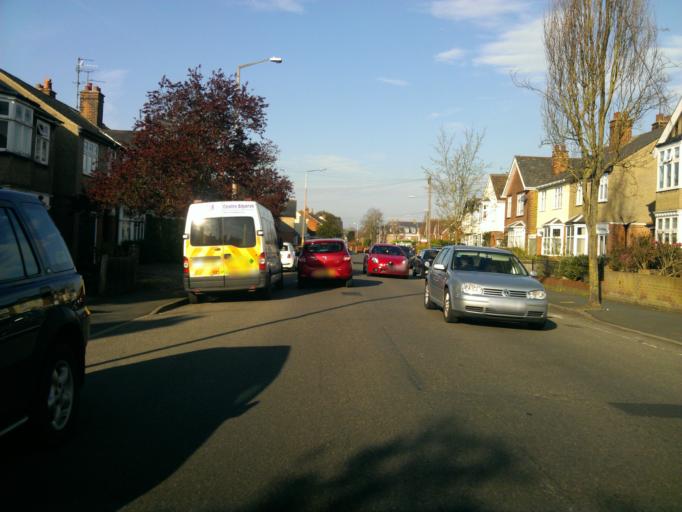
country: GB
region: England
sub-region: Essex
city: Colchester
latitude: 51.8800
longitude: 0.8834
